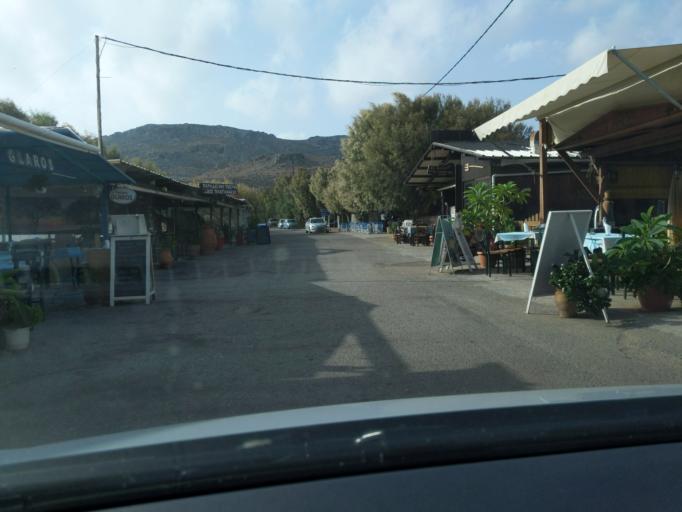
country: GR
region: Crete
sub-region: Nomos Lasithiou
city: Palekastro
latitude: 35.0977
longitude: 26.2632
